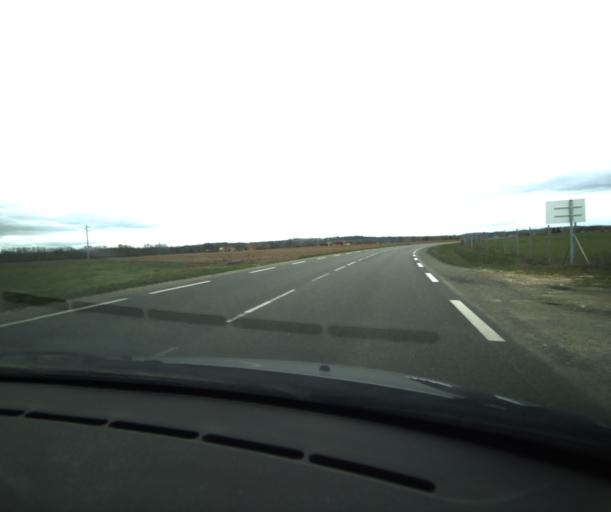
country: FR
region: Midi-Pyrenees
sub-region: Departement du Tarn-et-Garonne
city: Moissac
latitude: 44.0776
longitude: 1.1134
